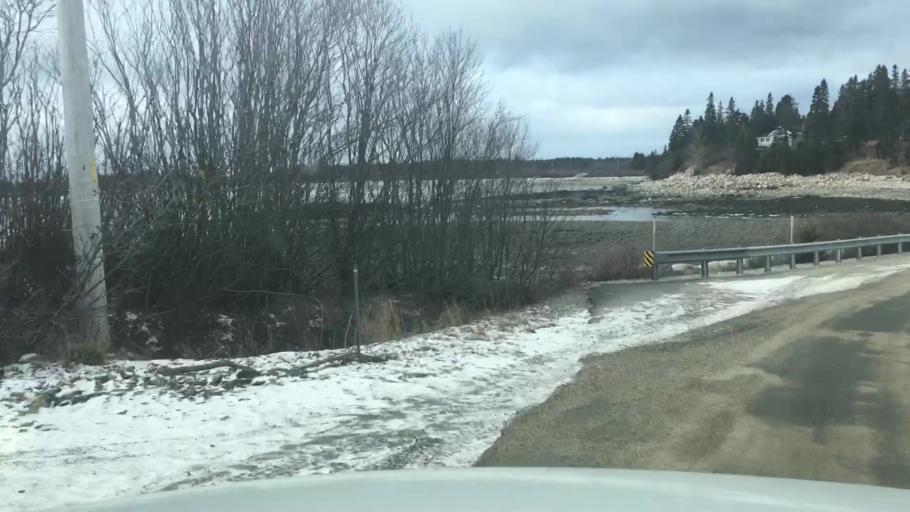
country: US
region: Maine
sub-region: Washington County
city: Machias
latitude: 44.6090
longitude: -67.4762
